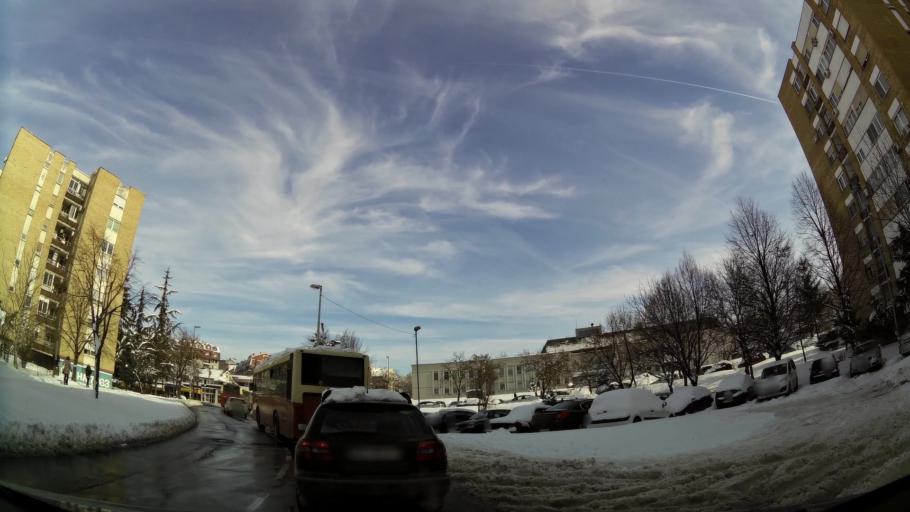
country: RS
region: Central Serbia
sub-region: Belgrade
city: Zvezdara
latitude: 44.7893
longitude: 20.5371
